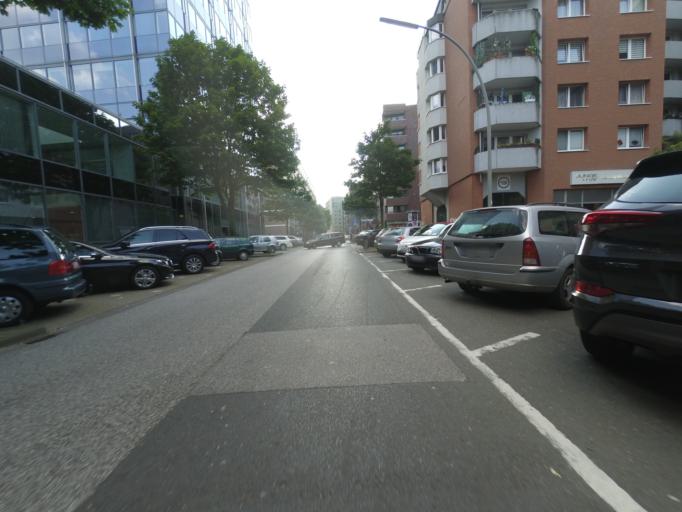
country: DE
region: Hamburg
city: Neustadt
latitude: 53.5505
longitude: 9.9784
